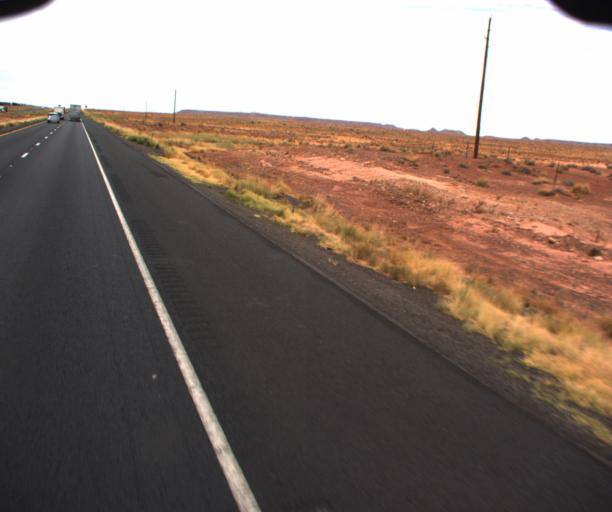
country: US
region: Arizona
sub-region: Coconino County
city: LeChee
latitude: 35.0532
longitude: -110.7862
